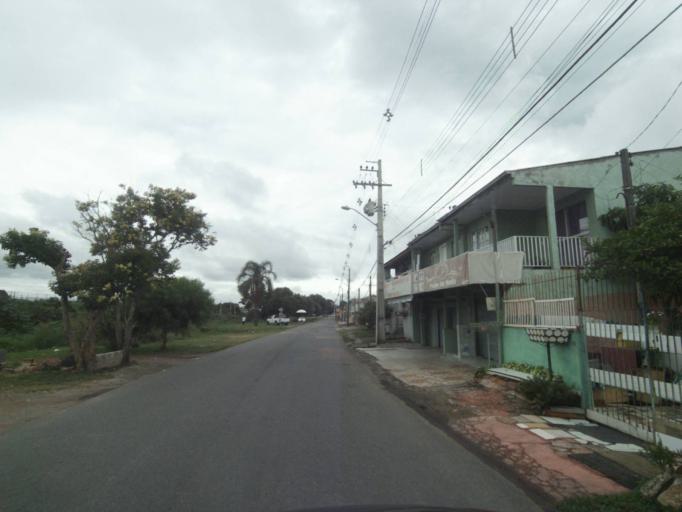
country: BR
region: Parana
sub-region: Curitiba
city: Curitiba
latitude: -25.4706
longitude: -49.3225
